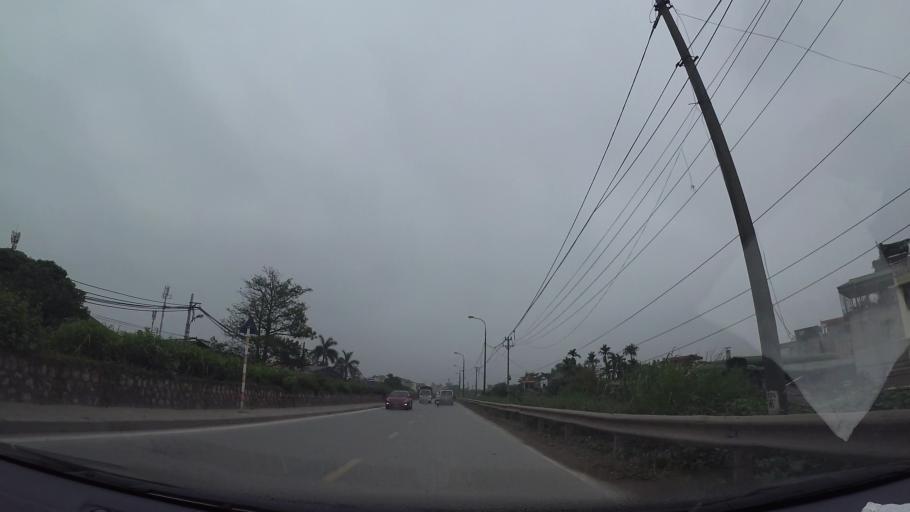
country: VN
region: Ha Noi
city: Hai BaTrung
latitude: 20.9917
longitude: 105.8925
